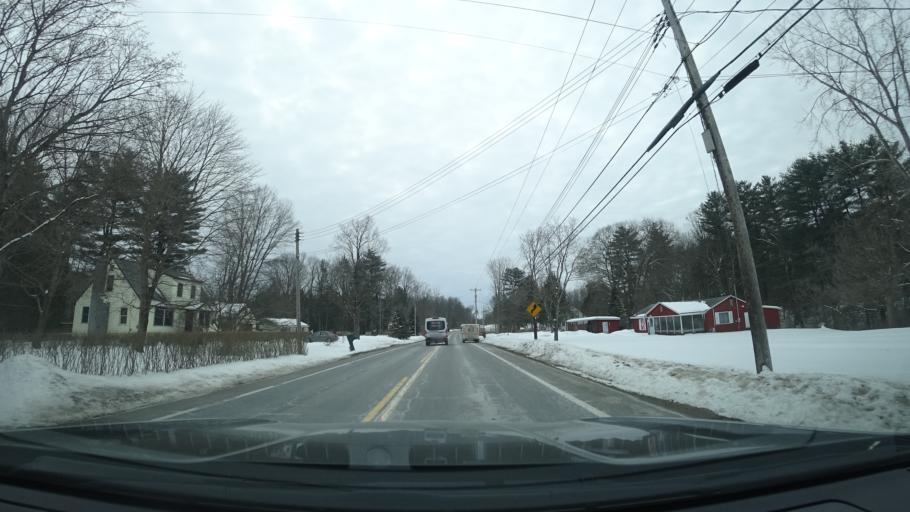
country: US
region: New York
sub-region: Washington County
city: Fort Edward
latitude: 43.2712
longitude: -73.6086
